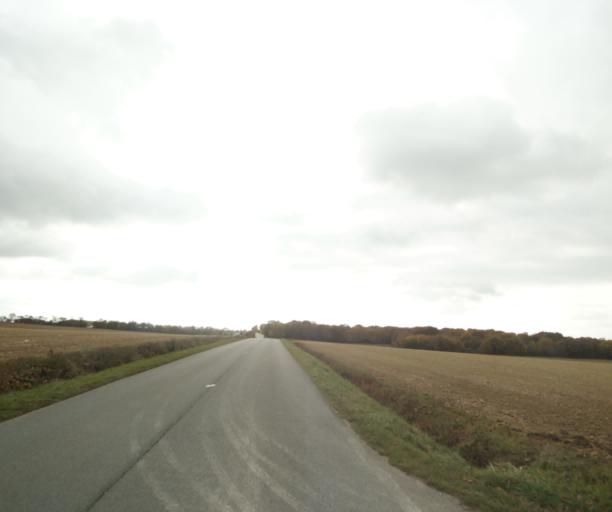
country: FR
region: Poitou-Charentes
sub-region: Departement de la Charente-Maritime
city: Saint-Georges-des-Coteaux
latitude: 45.7755
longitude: -0.7037
